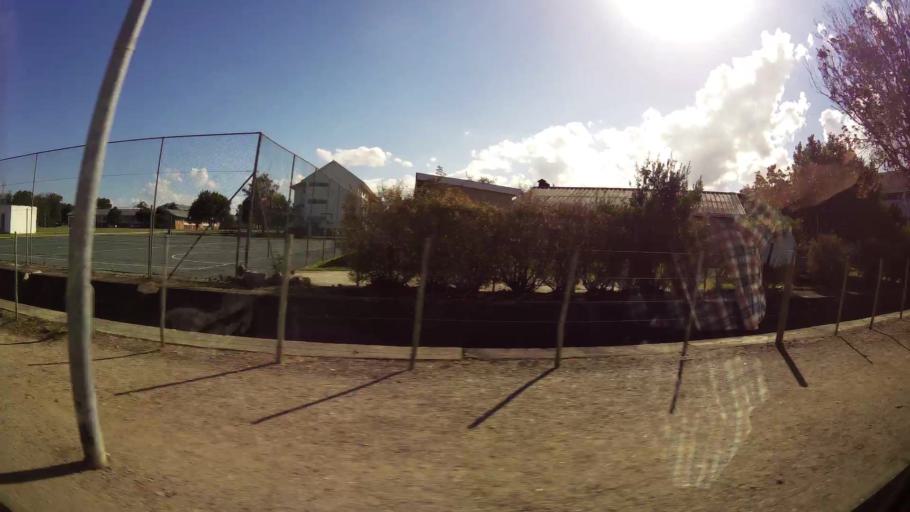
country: ZA
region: Western Cape
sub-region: Eden District Municipality
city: George
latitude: -33.9744
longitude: 22.4489
